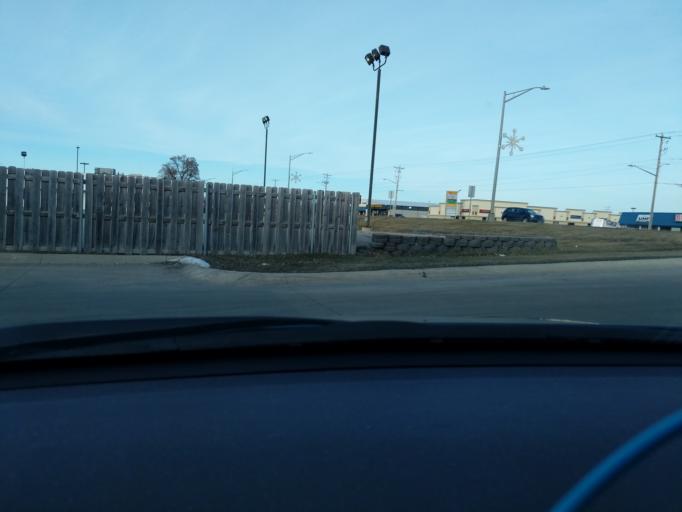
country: US
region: Minnesota
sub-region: Kandiyohi County
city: Willmar
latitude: 45.1068
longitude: -95.0432
